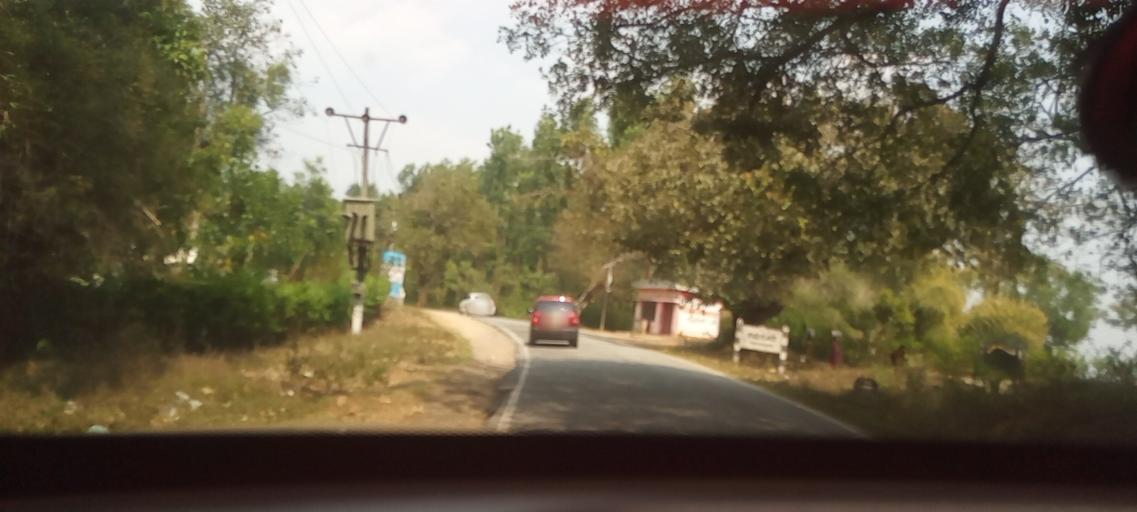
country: IN
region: Karnataka
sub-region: Chikmagalur
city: Chikmagalur
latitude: 13.2561
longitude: 75.6681
